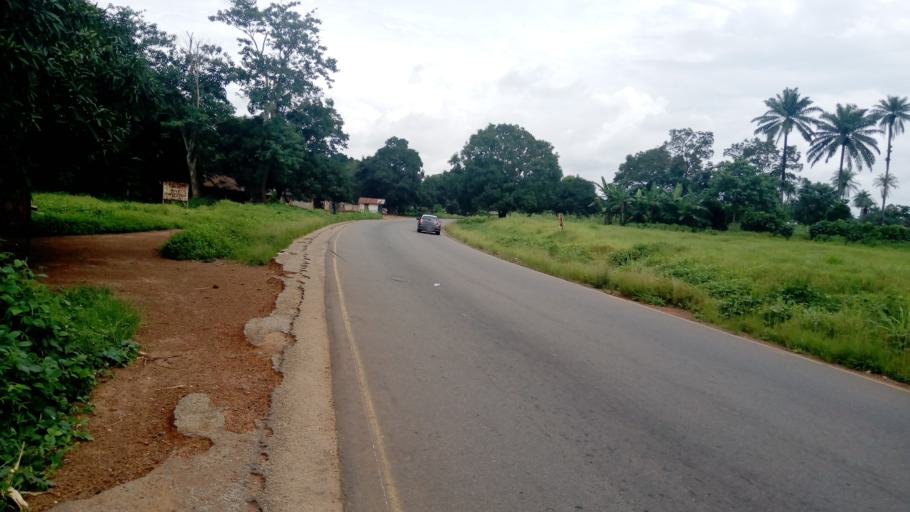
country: SL
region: Northern Province
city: Port Loko
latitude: 8.5056
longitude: -12.7607
